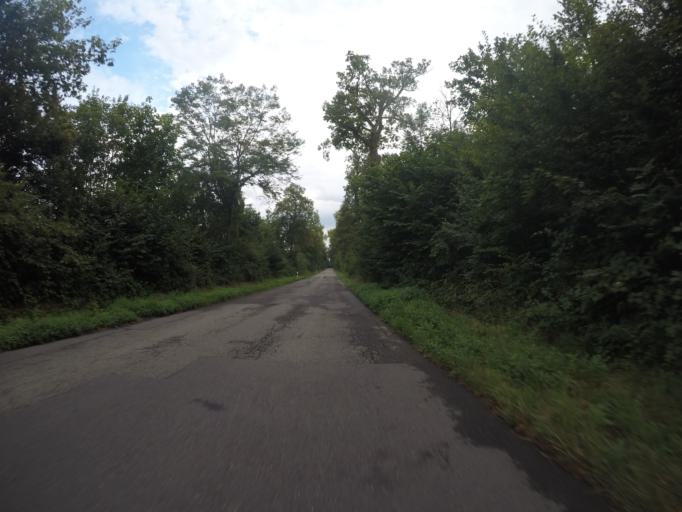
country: DE
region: Baden-Wuerttemberg
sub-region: Regierungsbezirk Stuttgart
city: Stuttgart-Ost
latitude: 48.7406
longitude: 9.1956
